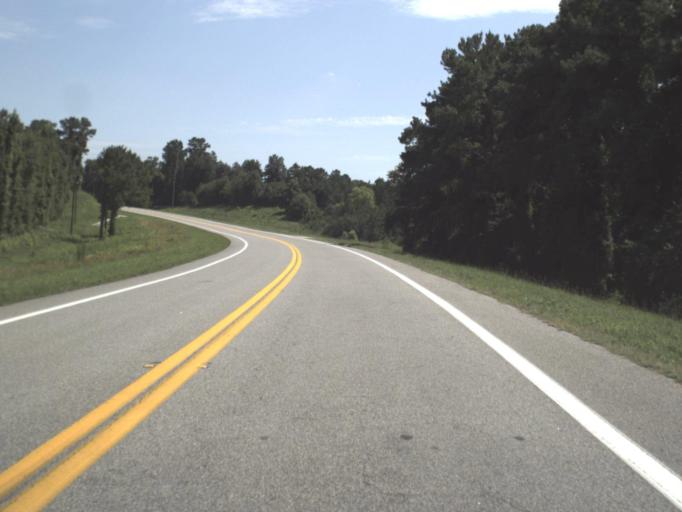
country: US
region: Florida
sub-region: Suwannee County
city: Live Oak
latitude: 30.4013
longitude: -82.9347
